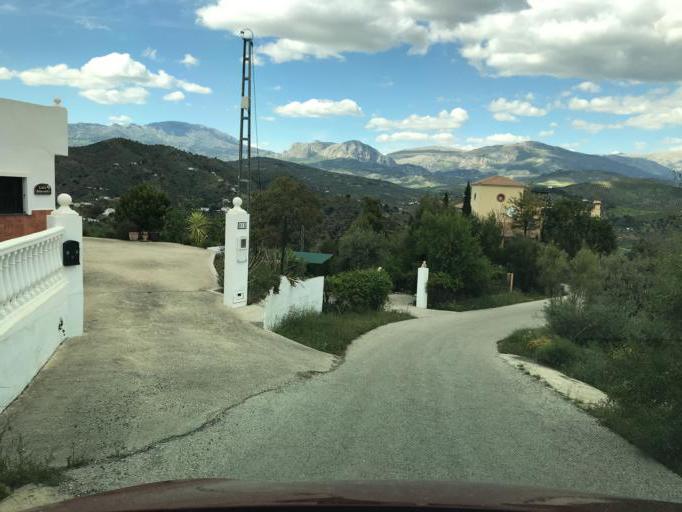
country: ES
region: Andalusia
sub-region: Provincia de Malaga
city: Comares
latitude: 36.8722
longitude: -4.2676
